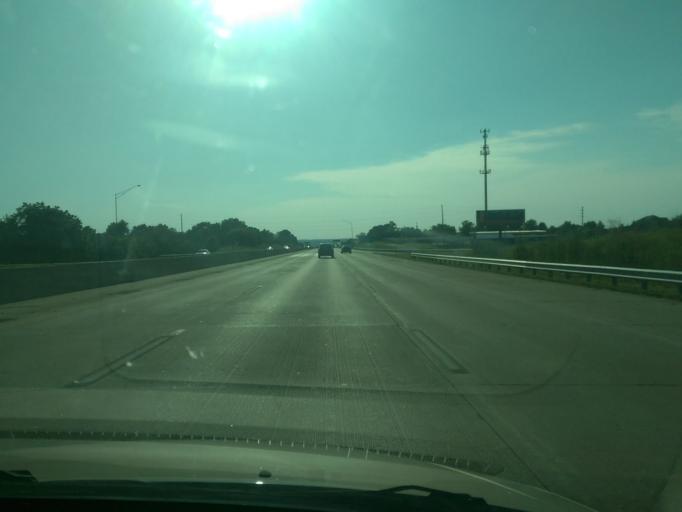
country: US
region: Missouri
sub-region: Jackson County
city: Blue Springs
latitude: 39.0345
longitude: -94.3068
